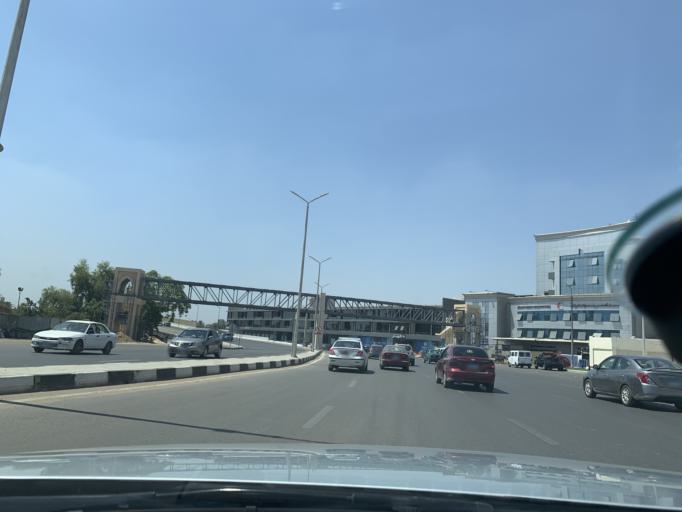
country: EG
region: Muhafazat al Qahirah
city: Cairo
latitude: 30.0909
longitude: 31.3486
